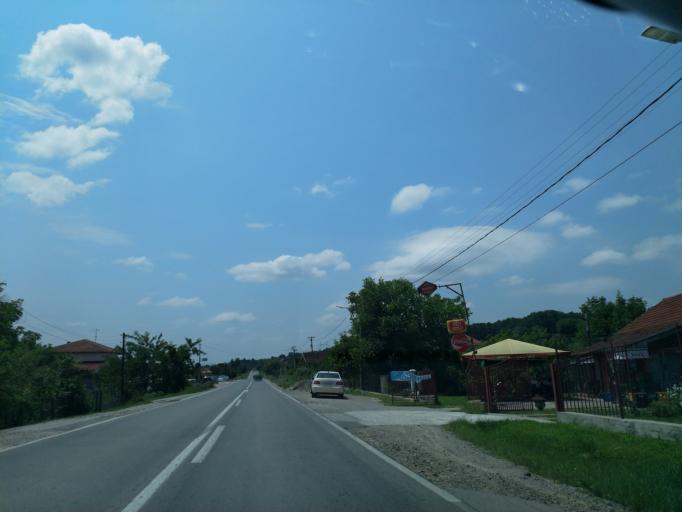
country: RS
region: Central Serbia
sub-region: Rasinski Okrug
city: Krusevac
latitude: 43.5335
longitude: 21.3221
